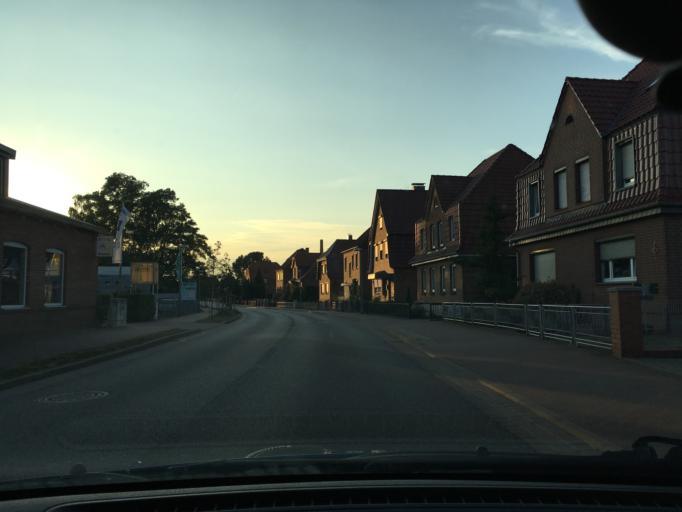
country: DE
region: Mecklenburg-Vorpommern
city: Boizenburg
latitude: 53.3781
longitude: 10.7573
